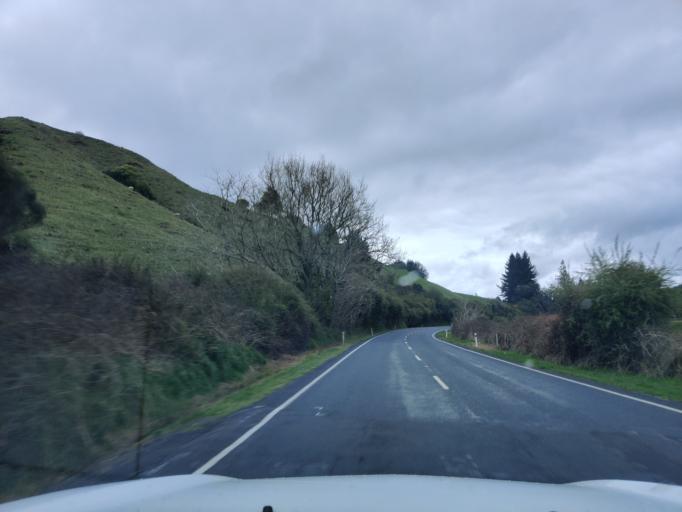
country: NZ
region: Waikato
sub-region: Otorohanga District
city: Otorohanga
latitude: -38.5918
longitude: 175.2185
